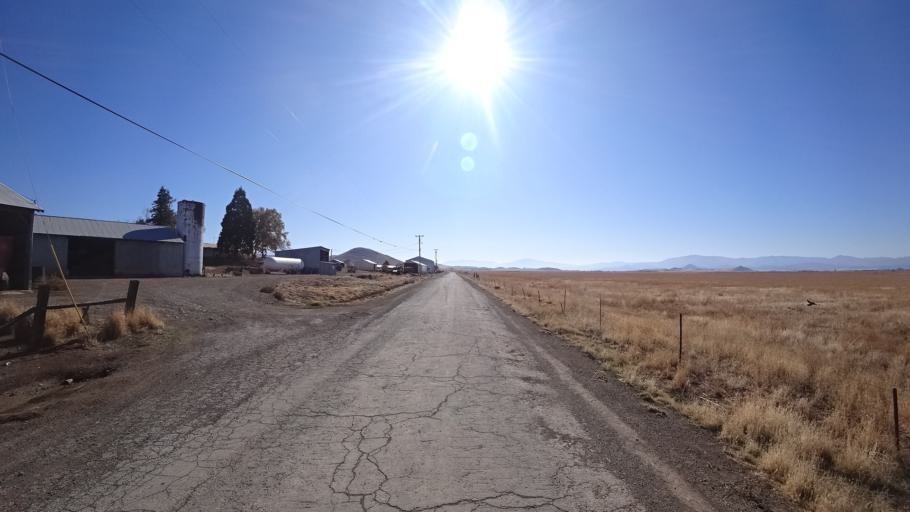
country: US
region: California
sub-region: Siskiyou County
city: Montague
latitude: 41.7921
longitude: -122.4342
